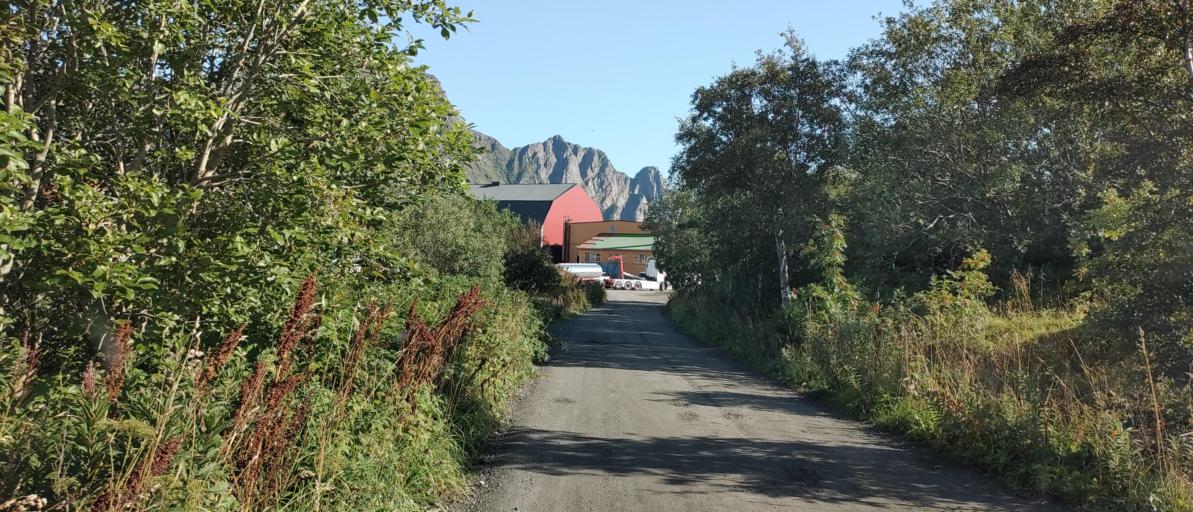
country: NO
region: Nordland
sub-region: Vagan
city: Svolvaer
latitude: 68.2285
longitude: 14.5705
